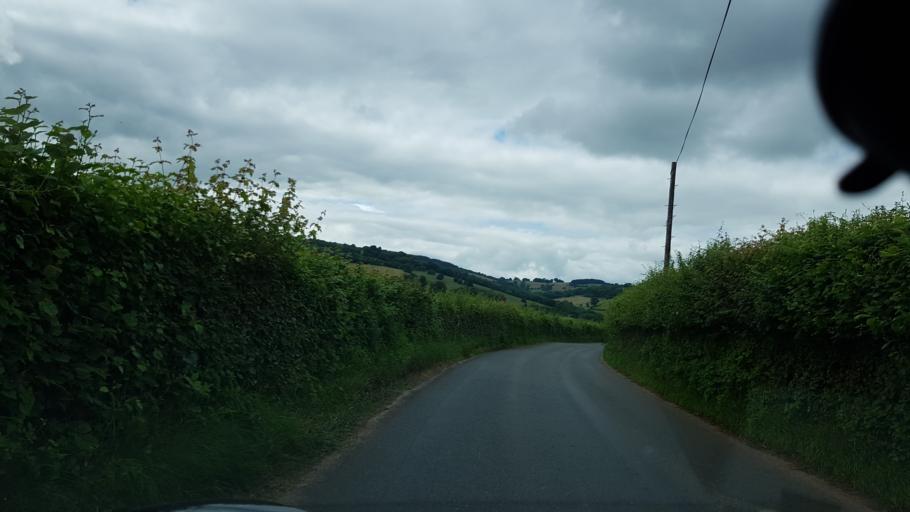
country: GB
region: England
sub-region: Herefordshire
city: Llanrothal
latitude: 51.8804
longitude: -2.8143
